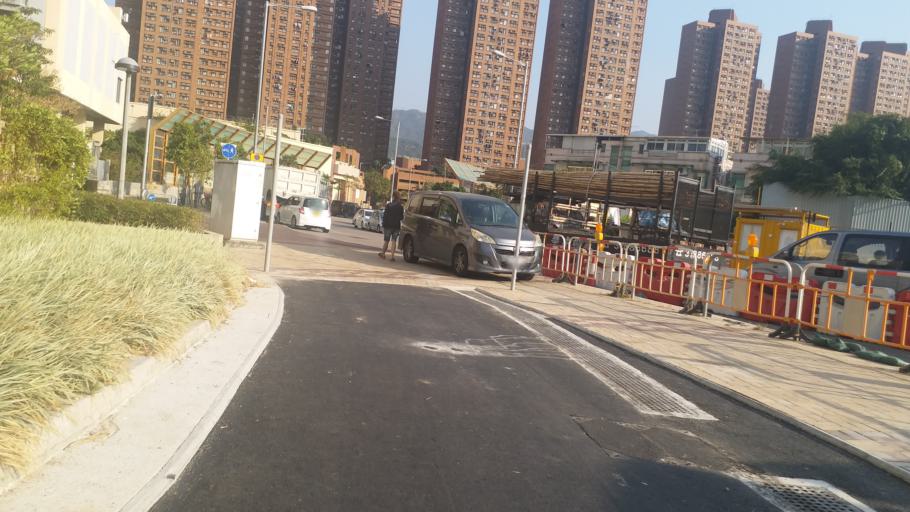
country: HK
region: Tuen Mun
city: Tuen Mun
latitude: 22.4140
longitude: 113.9752
